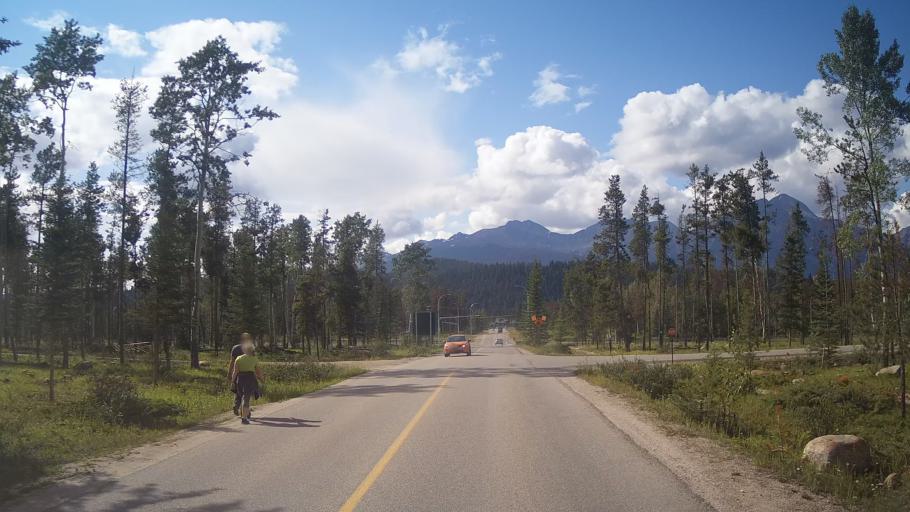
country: CA
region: Alberta
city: Jasper Park Lodge
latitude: 52.8683
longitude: -118.0737
